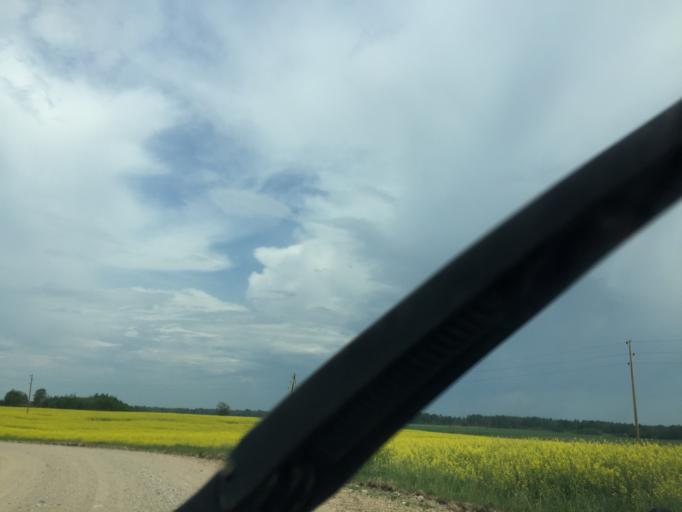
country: LV
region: Livani
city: Livani
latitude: 56.5779
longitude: 26.1775
